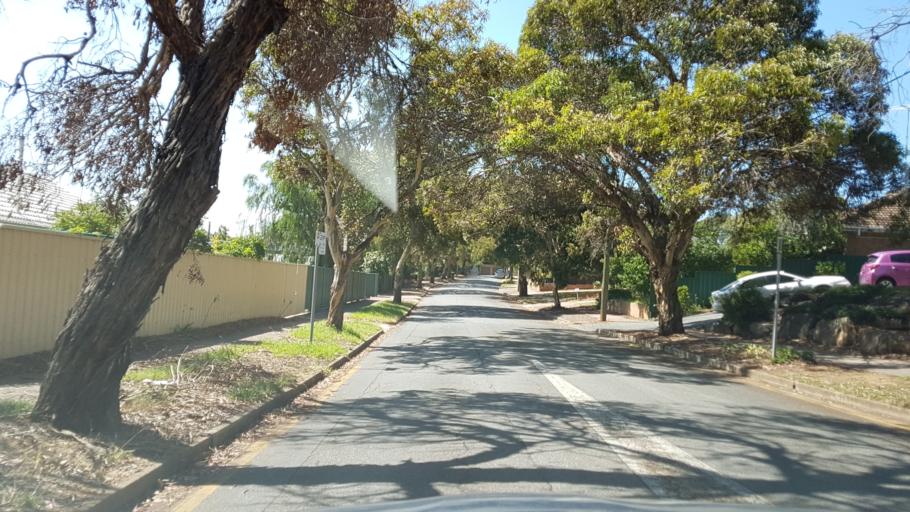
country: AU
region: South Australia
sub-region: Marion
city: Marion
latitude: -35.0238
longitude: 138.5643
